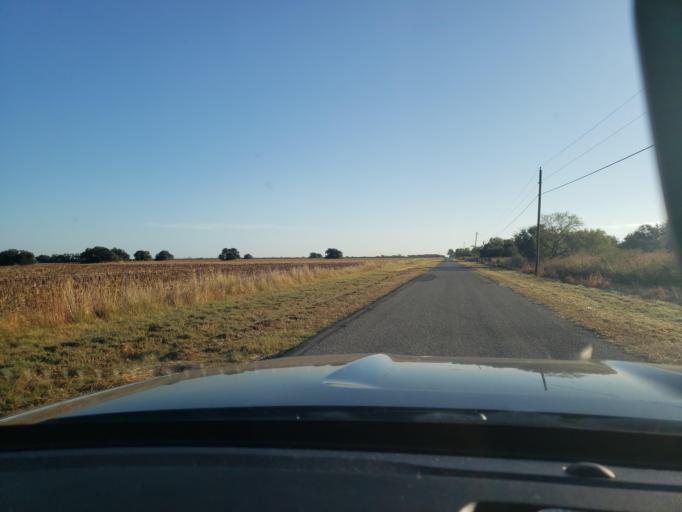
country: US
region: Texas
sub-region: Bee County
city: Beeville
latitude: 28.4279
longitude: -97.6962
